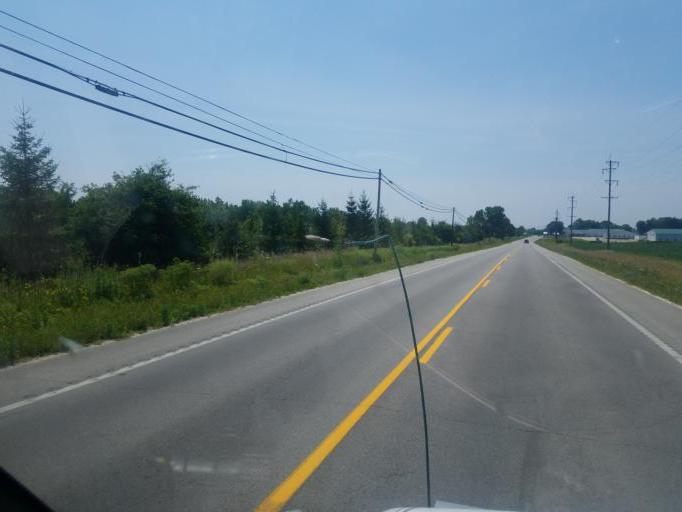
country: US
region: Ohio
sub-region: Auglaize County
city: Saint Marys
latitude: 40.5510
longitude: -84.4586
